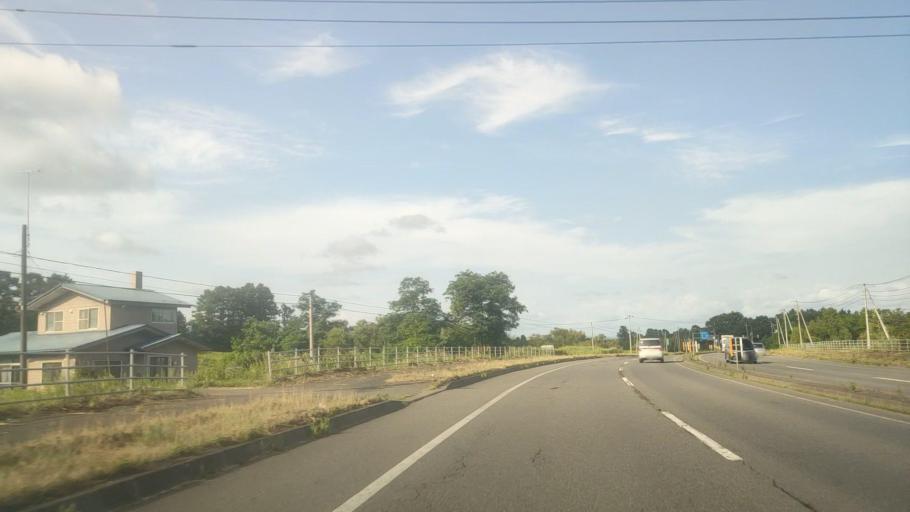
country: JP
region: Hokkaido
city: Chitose
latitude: 42.7753
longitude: 141.8278
